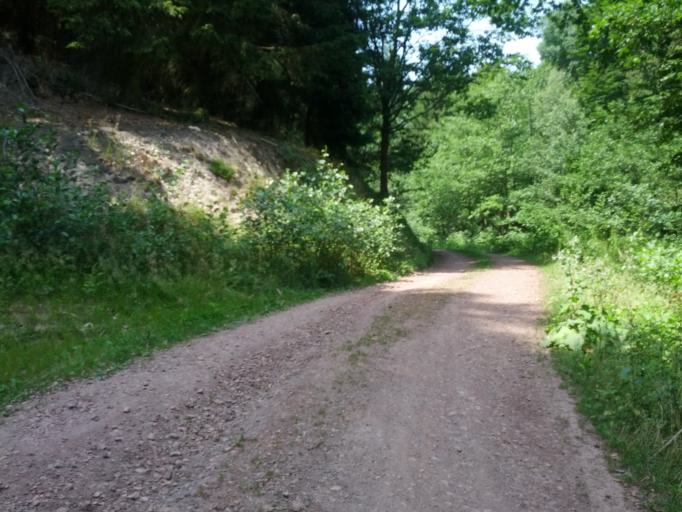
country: DE
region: Thuringia
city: Eisenach
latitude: 50.9528
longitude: 10.3435
